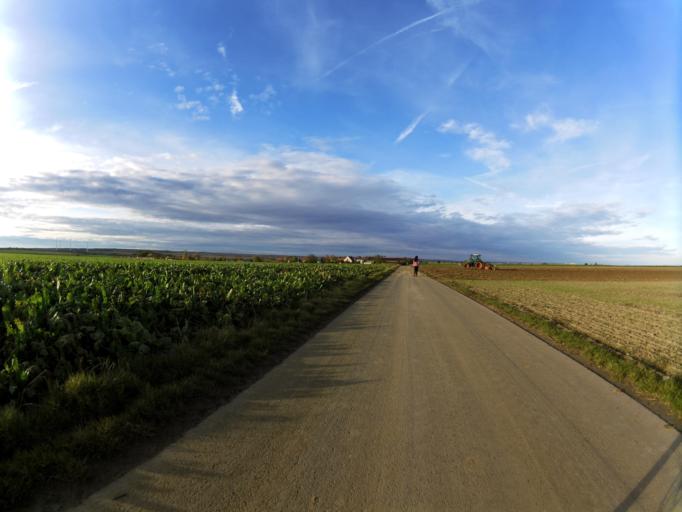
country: DE
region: Bavaria
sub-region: Regierungsbezirk Unterfranken
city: Geroldshausen
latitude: 49.6886
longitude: 9.9367
